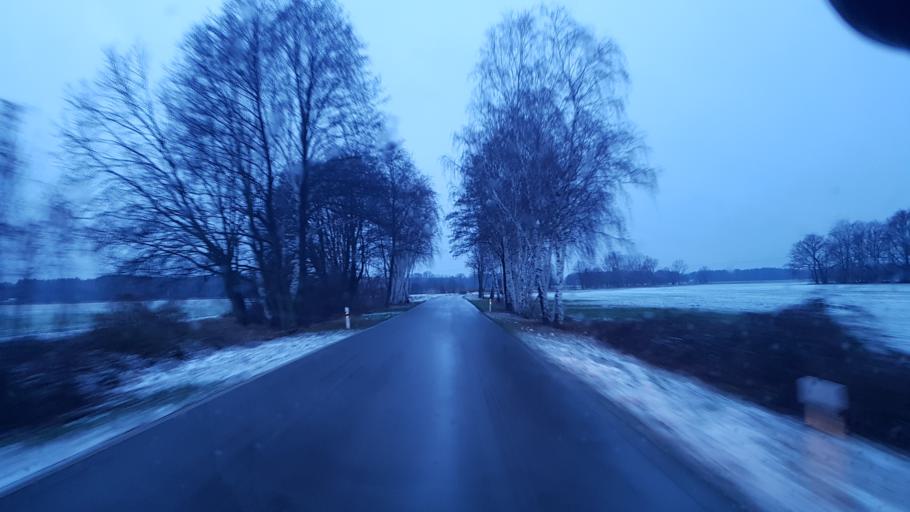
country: DE
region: Brandenburg
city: Drehnow
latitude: 51.8255
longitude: 14.3790
